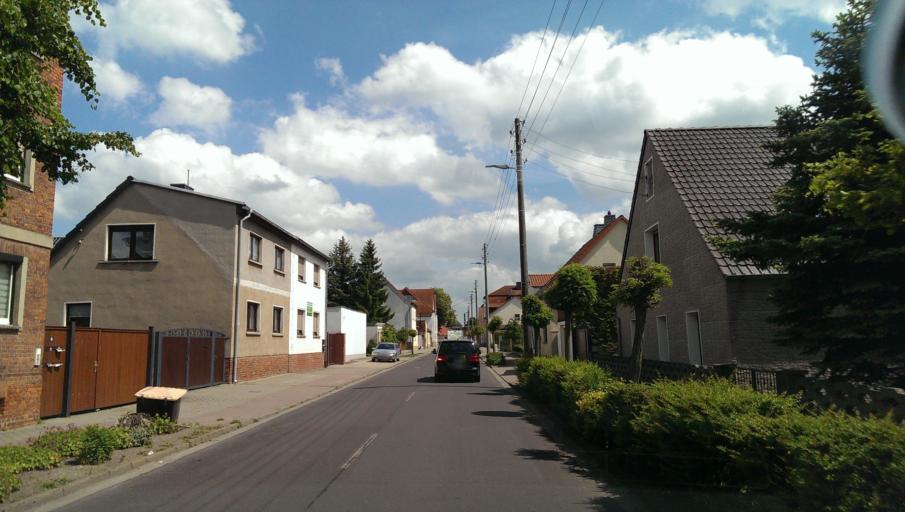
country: DE
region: Saxony-Anhalt
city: Plotzky
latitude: 52.0461
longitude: 11.8219
